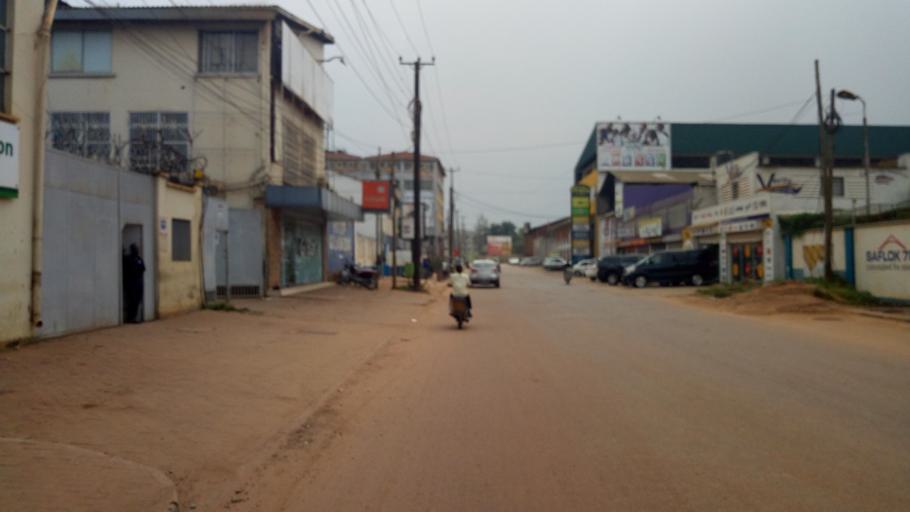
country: UG
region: Central Region
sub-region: Kampala District
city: Kampala
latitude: 0.3142
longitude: 32.6132
